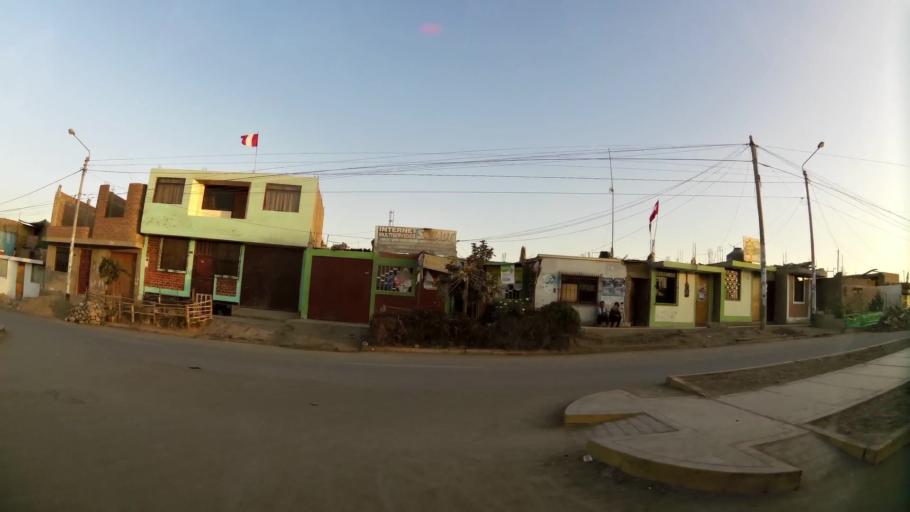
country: PE
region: Ica
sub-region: Provincia de Pisco
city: San Clemente
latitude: -13.6774
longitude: -76.1531
